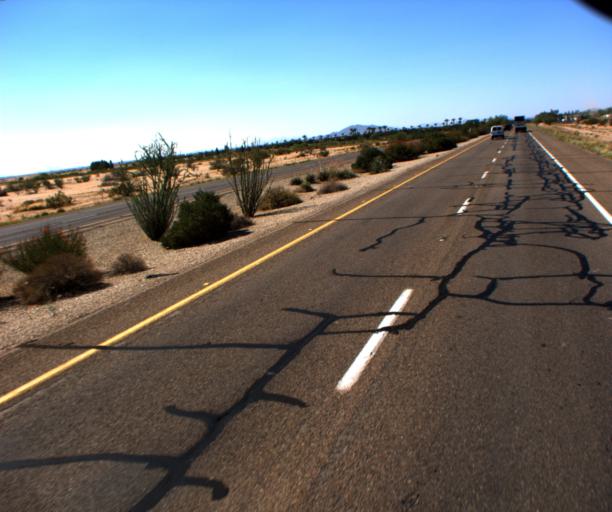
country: US
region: Arizona
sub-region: Pinal County
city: Casa Grande
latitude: 32.9632
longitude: -111.7569
